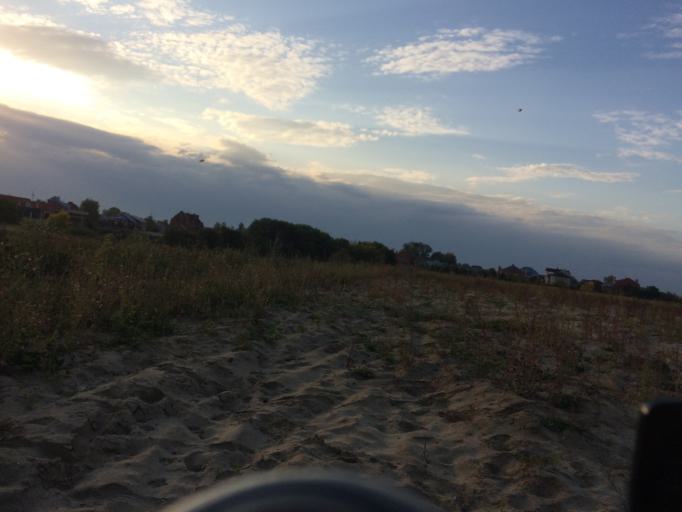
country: RU
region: Mariy-El
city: Yoshkar-Ola
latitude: 56.6479
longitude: 47.9231
